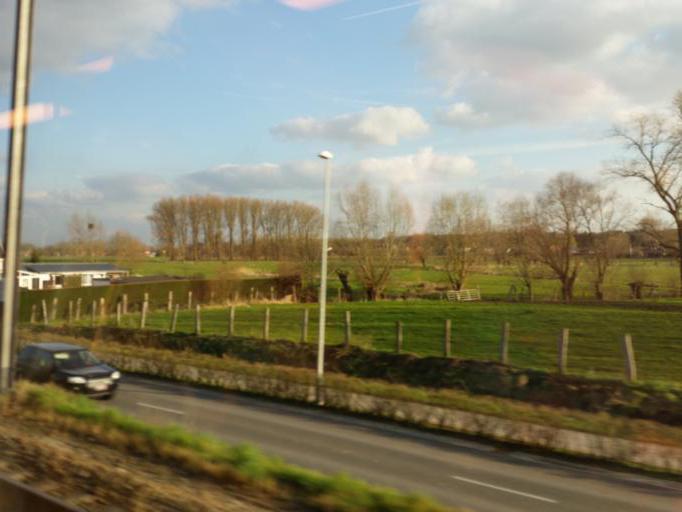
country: BE
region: Flanders
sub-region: Provincie Oost-Vlaanderen
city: Buggenhout
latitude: 51.0156
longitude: 4.2111
